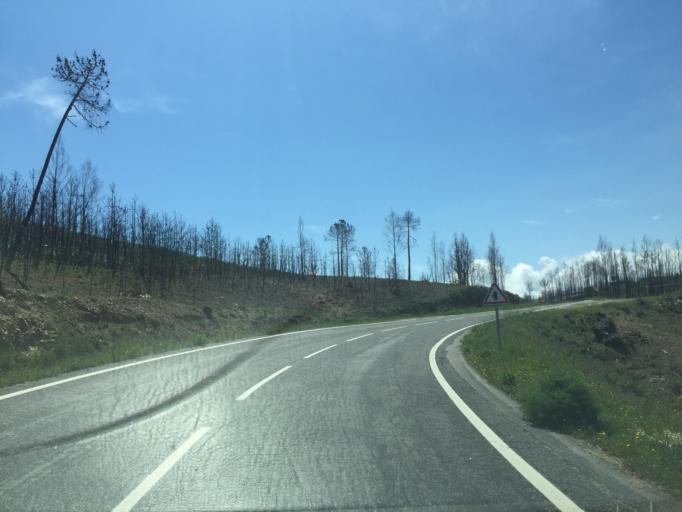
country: PT
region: Coimbra
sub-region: Pampilhosa da Serra
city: Pampilhosa da Serra
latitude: 40.0241
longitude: -7.9655
